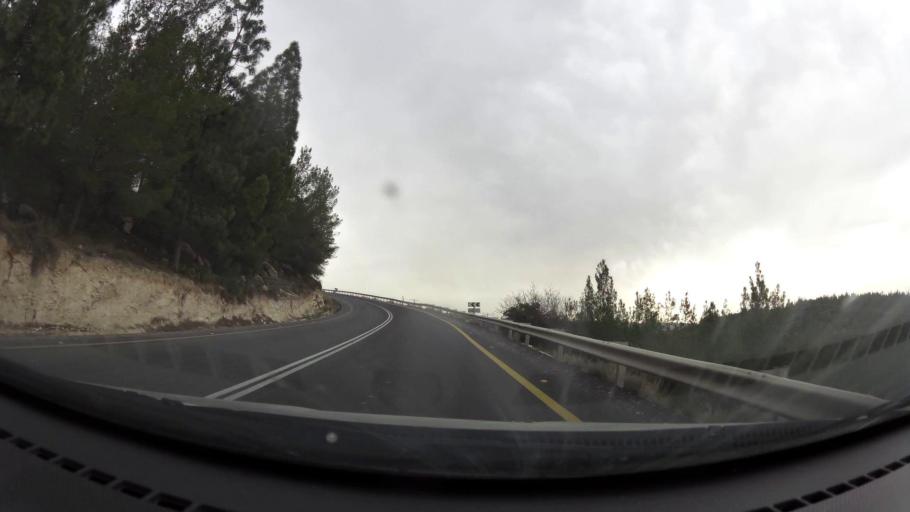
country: PS
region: West Bank
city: Surif
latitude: 31.6742
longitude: 35.0250
